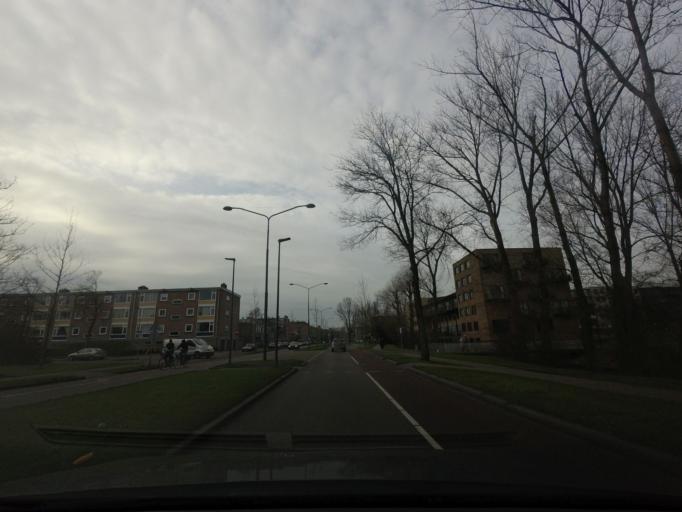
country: NL
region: North Holland
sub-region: Gemeente Alkmaar
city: Alkmaar
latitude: 52.6183
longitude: 4.7567
